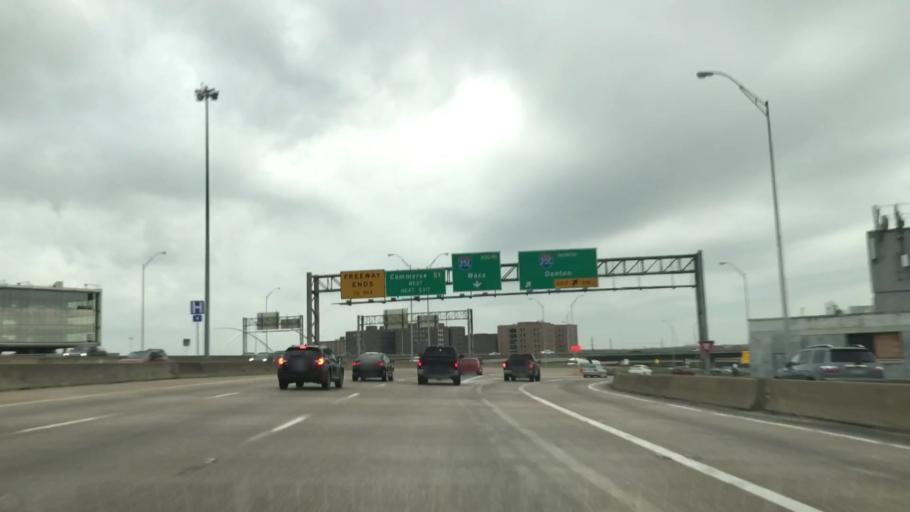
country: US
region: Texas
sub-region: Dallas County
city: Dallas
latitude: 32.7836
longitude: -96.8086
